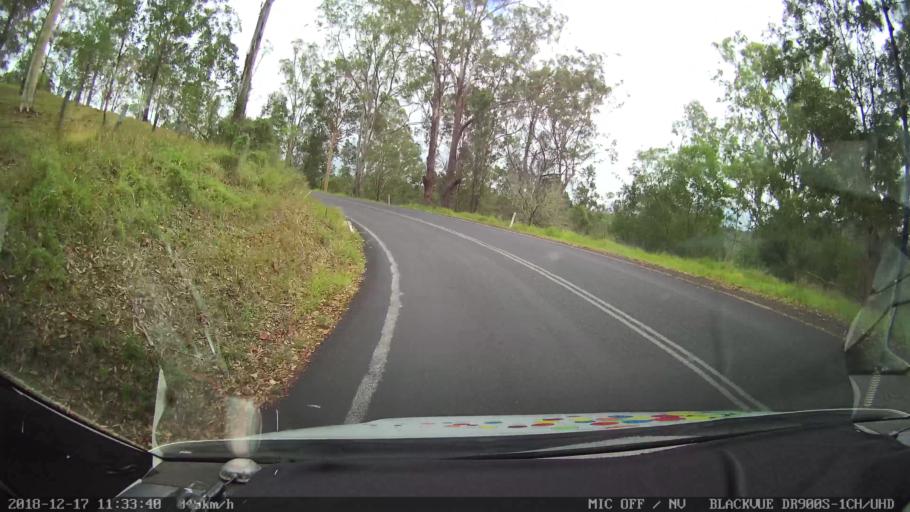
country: AU
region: New South Wales
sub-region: Kyogle
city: Kyogle
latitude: -28.7300
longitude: 152.6181
